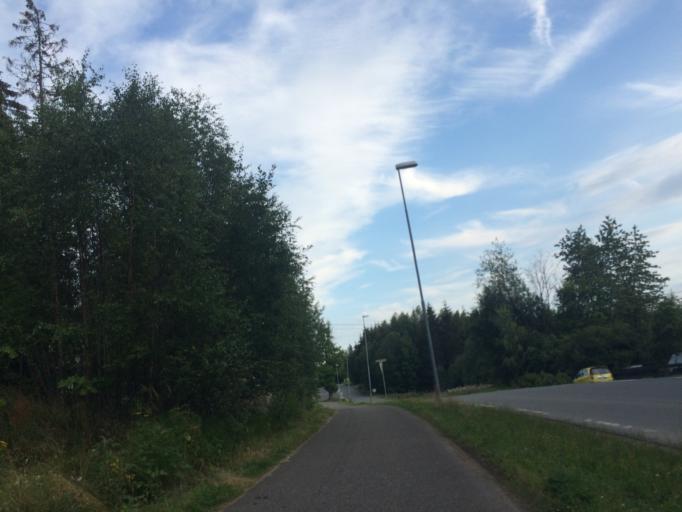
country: NO
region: Akershus
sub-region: Ski
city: Ski
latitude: 59.7022
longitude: 10.8444
